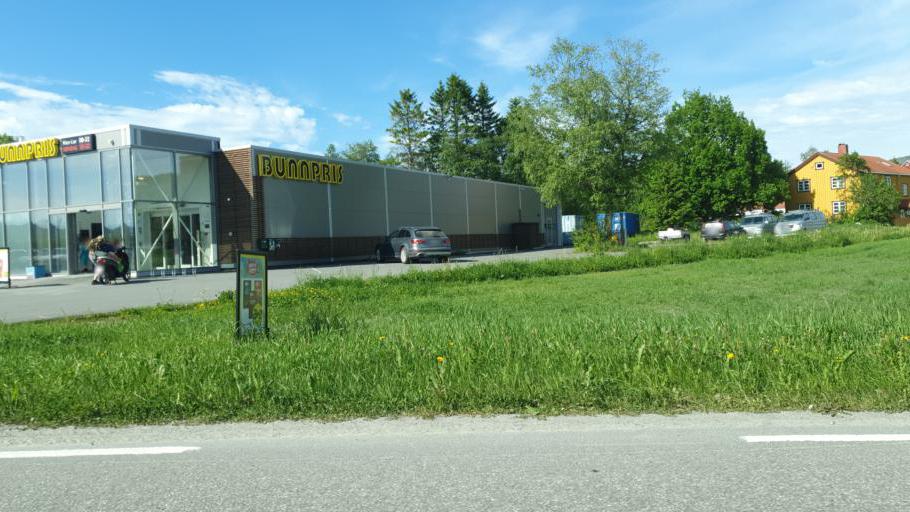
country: NO
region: Sor-Trondelag
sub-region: Rissa
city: Rissa
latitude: 63.5107
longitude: 10.0152
